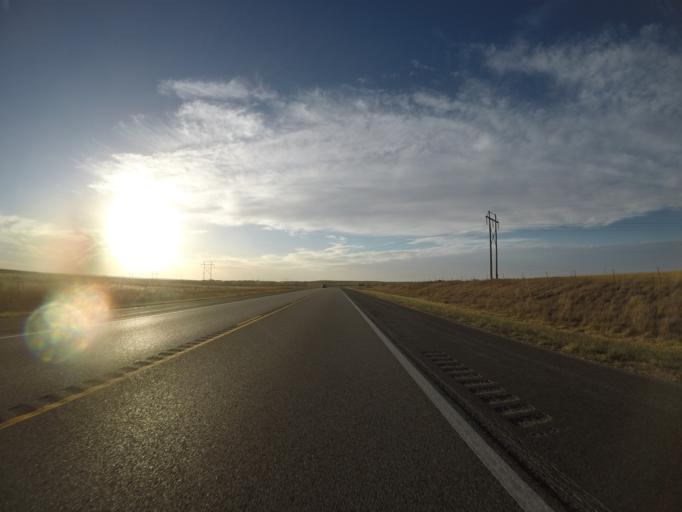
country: US
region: Kansas
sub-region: Chase County
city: Cottonwood Falls
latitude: 38.4057
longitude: -96.4774
